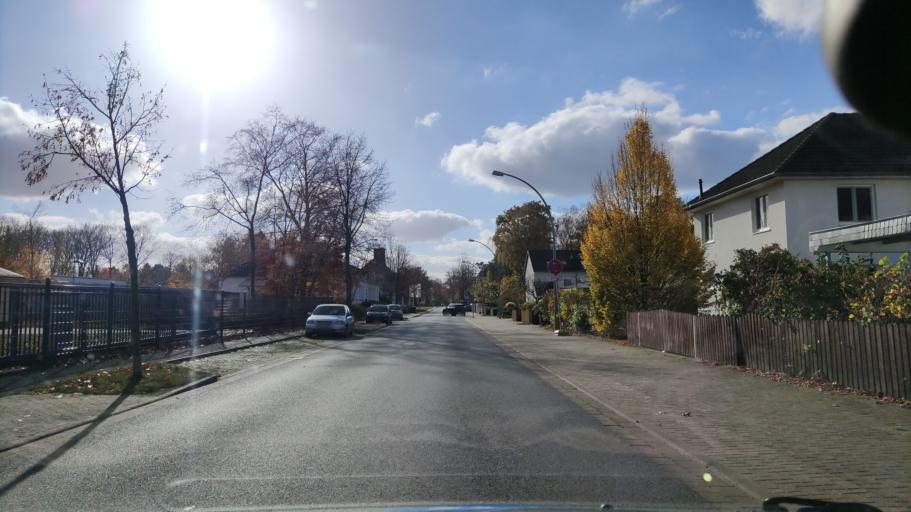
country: DE
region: Lower Saxony
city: Munster
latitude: 52.9985
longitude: 10.1146
